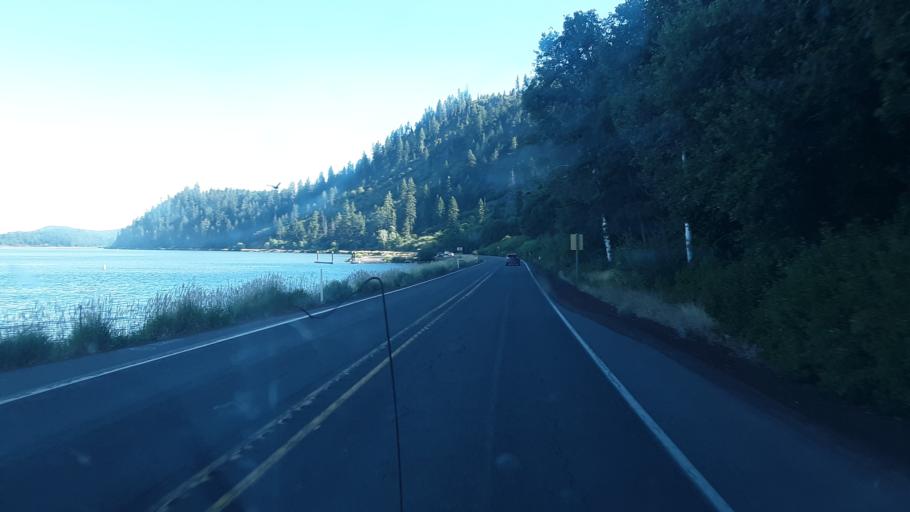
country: US
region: Oregon
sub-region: Klamath County
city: Klamath Falls
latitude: 42.3164
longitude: -121.9424
